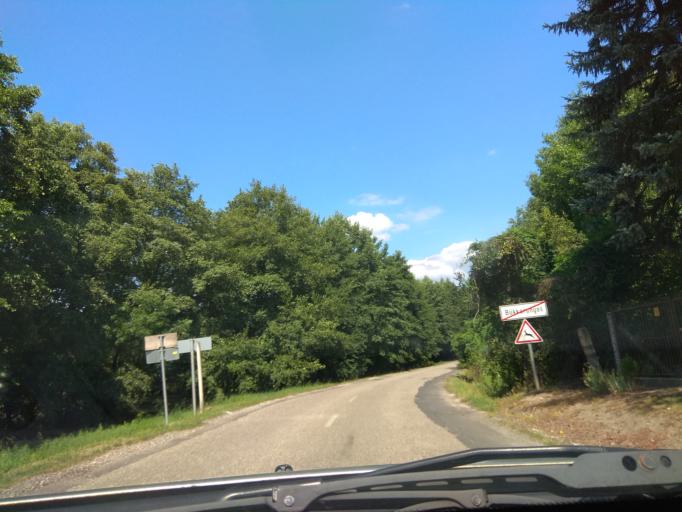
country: HU
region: Borsod-Abauj-Zemplen
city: Harsany
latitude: 47.9940
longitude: 20.7629
